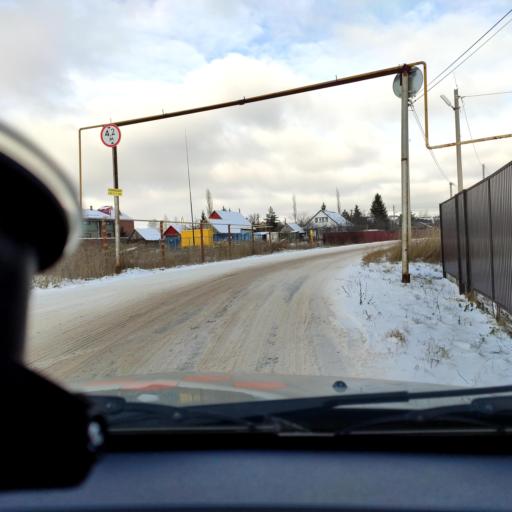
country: RU
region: Bashkortostan
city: Avdon
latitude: 54.7839
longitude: 55.7281
